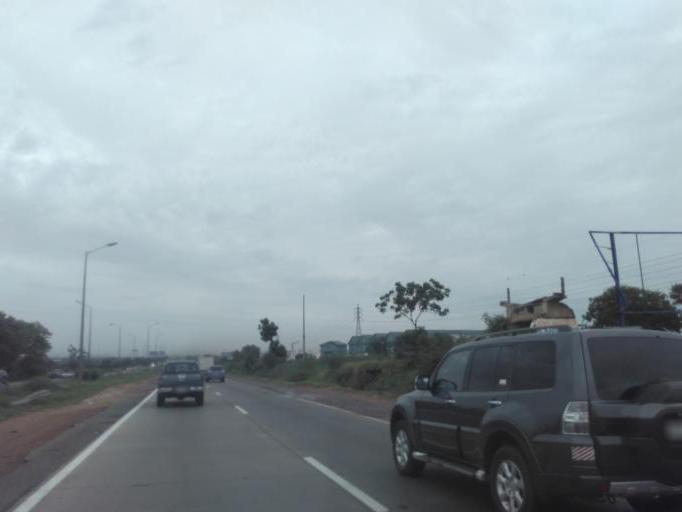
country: GH
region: Greater Accra
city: Tema
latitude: 5.6625
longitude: -0.0709
